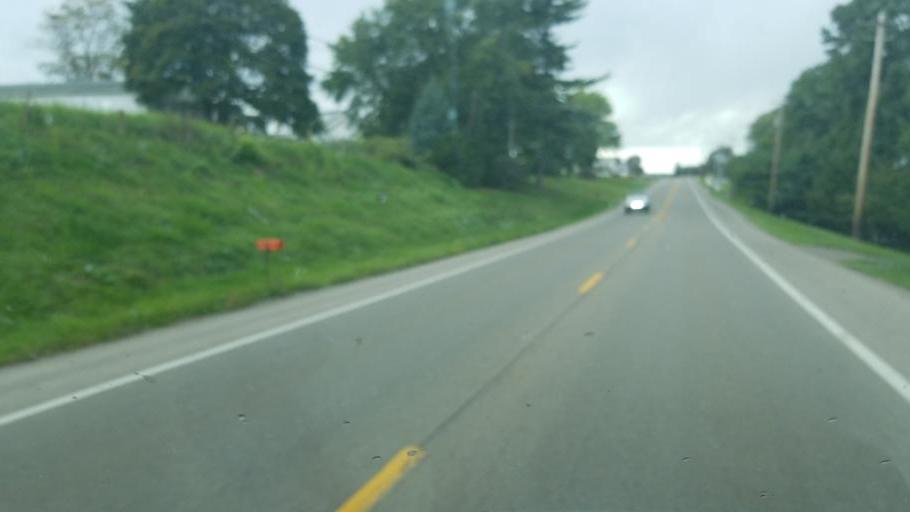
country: US
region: Ohio
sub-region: Tuscarawas County
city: Sugarcreek
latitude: 40.5456
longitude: -81.7402
